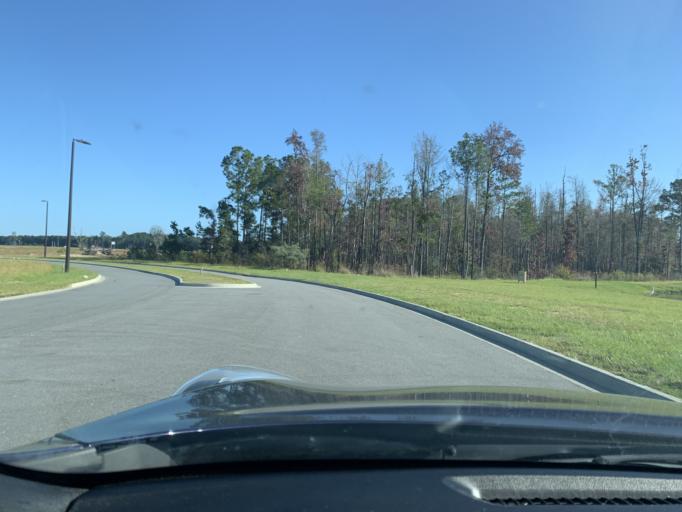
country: US
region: Georgia
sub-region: Chatham County
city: Pooler
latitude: 32.0744
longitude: -81.2779
